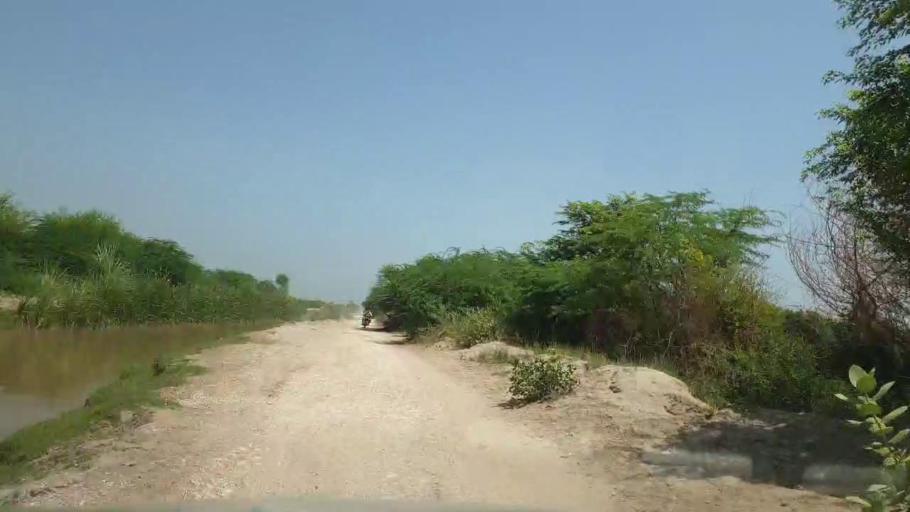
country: PK
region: Sindh
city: Rohri
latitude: 27.6327
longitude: 69.1000
